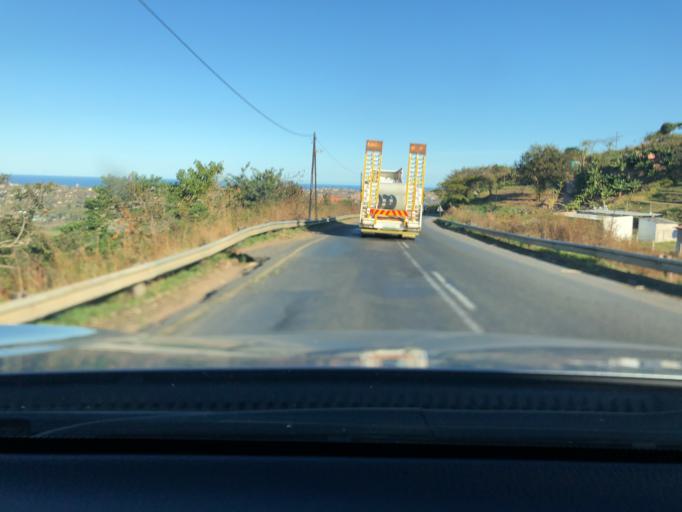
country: ZA
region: KwaZulu-Natal
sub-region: eThekwini Metropolitan Municipality
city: Umkomaas
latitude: -30.0222
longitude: 30.8109
